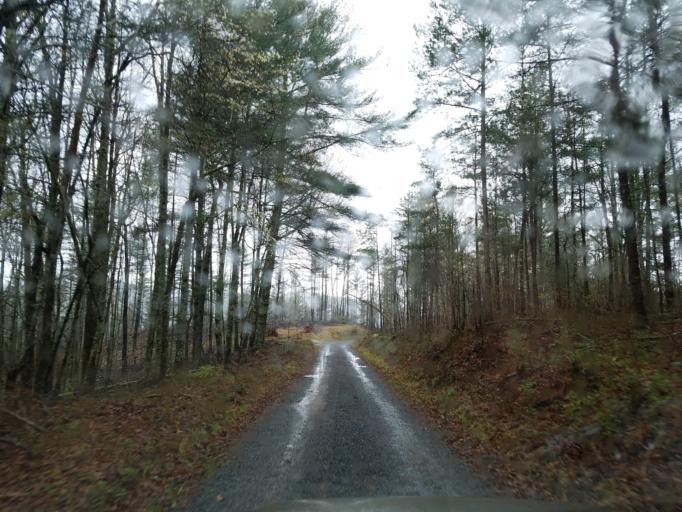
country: US
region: Georgia
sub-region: Fannin County
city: Blue Ridge
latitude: 34.8388
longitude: -84.2347
